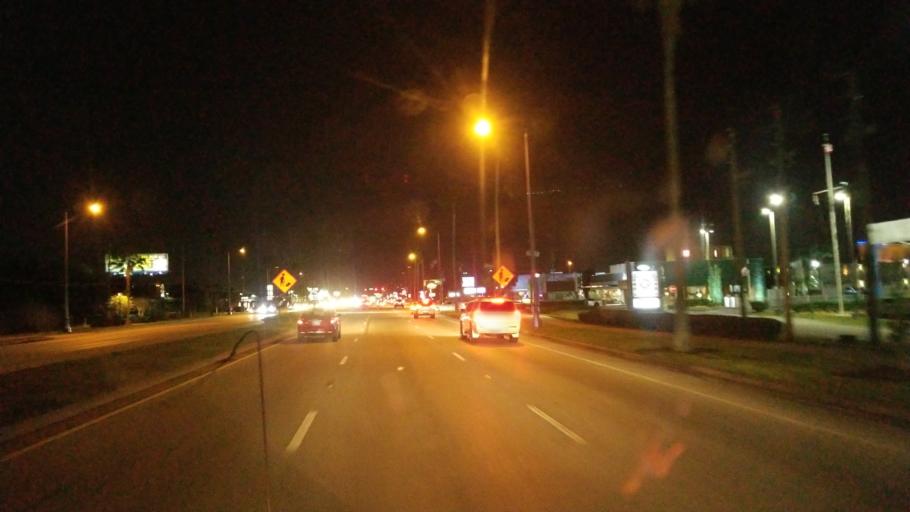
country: US
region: Florida
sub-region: Osceola County
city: Celebration
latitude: 28.3329
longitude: -81.4932
